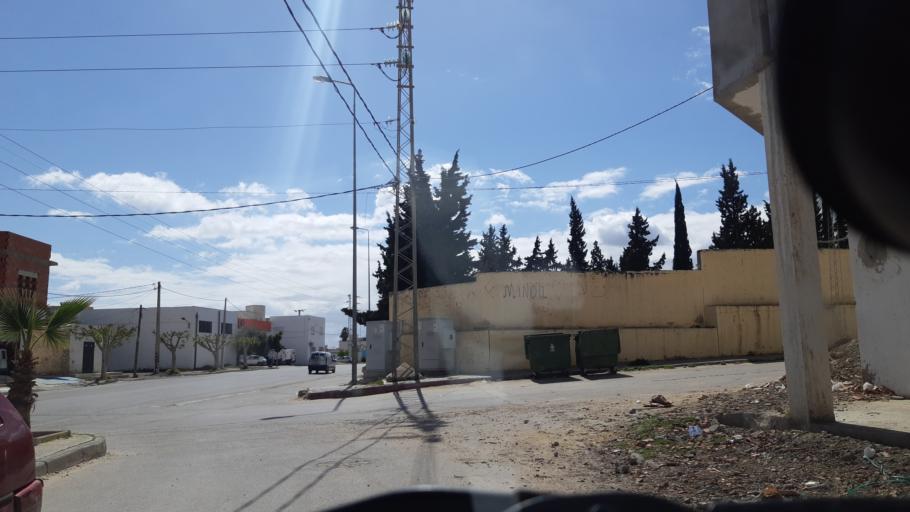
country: TN
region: Susah
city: Akouda
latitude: 35.8914
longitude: 10.5349
